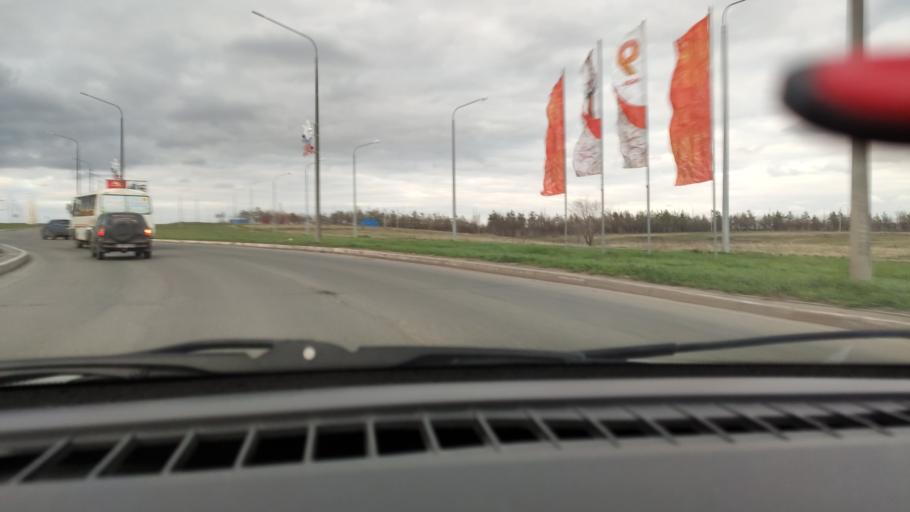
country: RU
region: Orenburg
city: Orenburg
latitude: 51.8099
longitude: 55.1800
